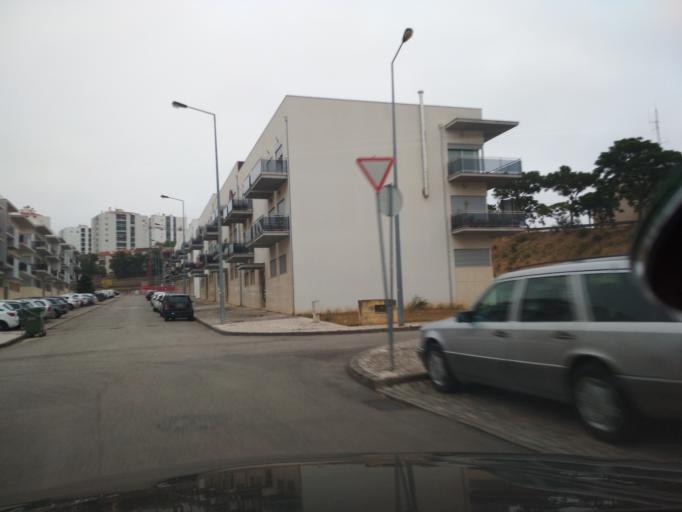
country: PT
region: Coimbra
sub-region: Coimbra
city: Coimbra
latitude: 40.1945
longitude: -8.4014
